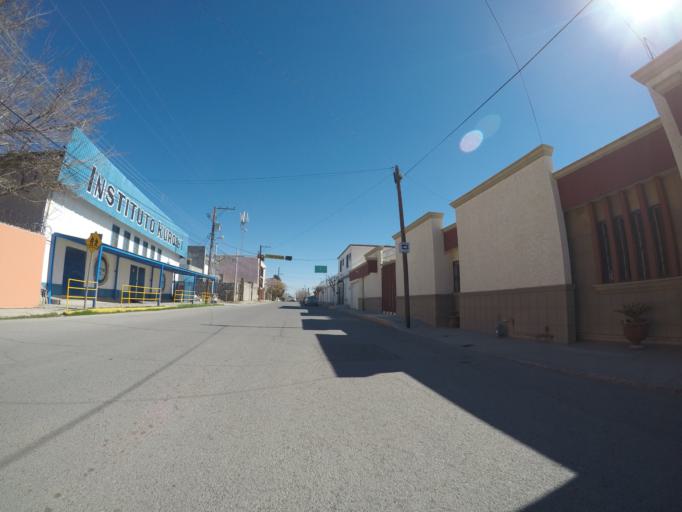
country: MX
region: Chihuahua
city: Ciudad Juarez
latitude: 31.7325
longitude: -106.4467
